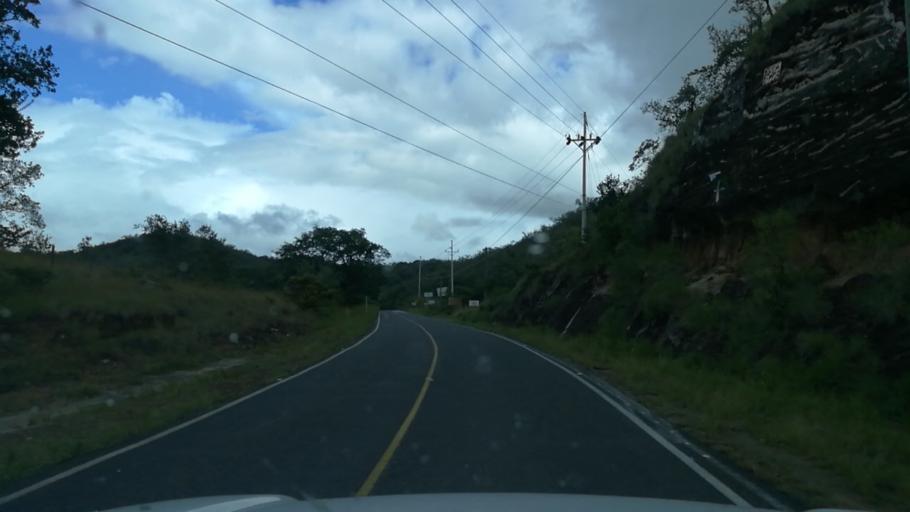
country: CR
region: Guanacaste
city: Fortuna
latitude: 10.6332
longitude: -85.2304
